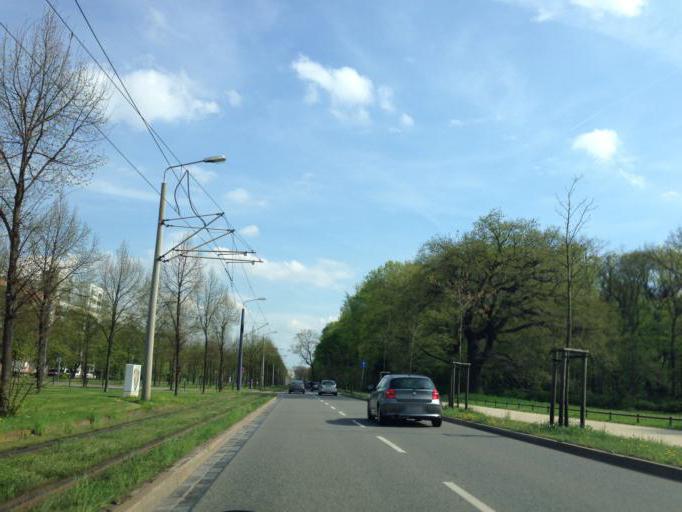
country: DE
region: Saxony
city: Dresden
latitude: 51.0437
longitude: 13.7611
